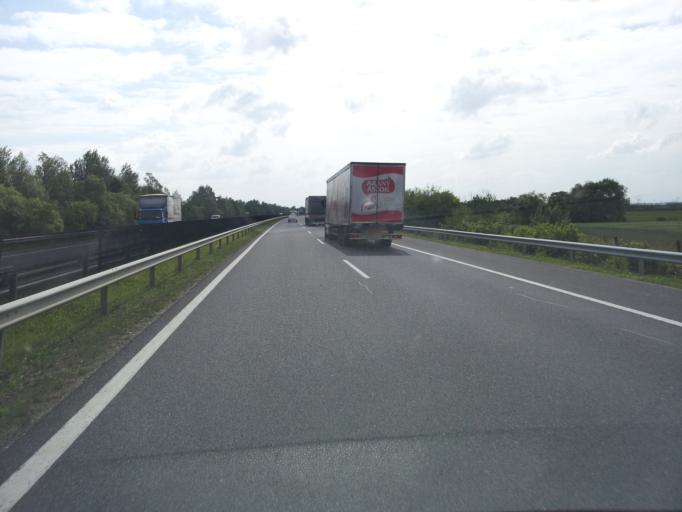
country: HU
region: Borsod-Abauj-Zemplen
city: Hejobaba
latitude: 47.8725
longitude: 20.9596
